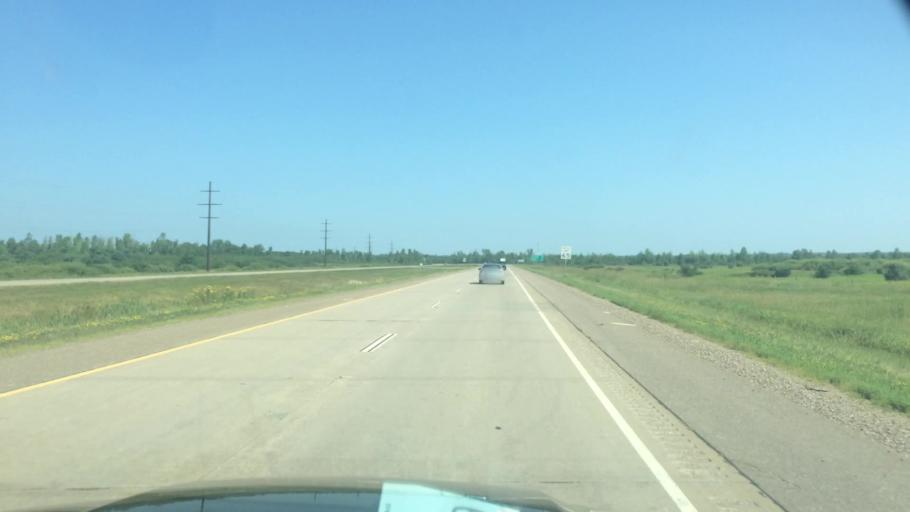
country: US
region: Wisconsin
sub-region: Lincoln County
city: Merrill
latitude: 45.2209
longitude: -89.6707
